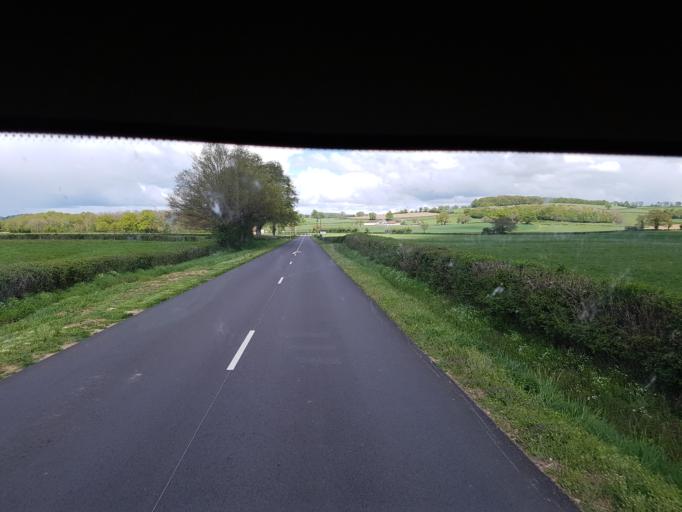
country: FR
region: Bourgogne
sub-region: Departement de Saone-et-Loire
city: Etang-sur-Arroux
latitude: 46.8427
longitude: 4.1945
